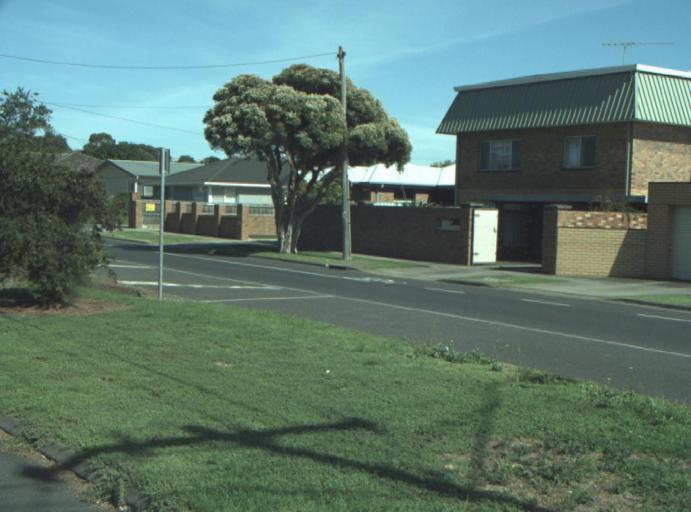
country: AU
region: Victoria
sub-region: Greater Geelong
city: Bell Park
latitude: -38.0989
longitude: 144.3336
